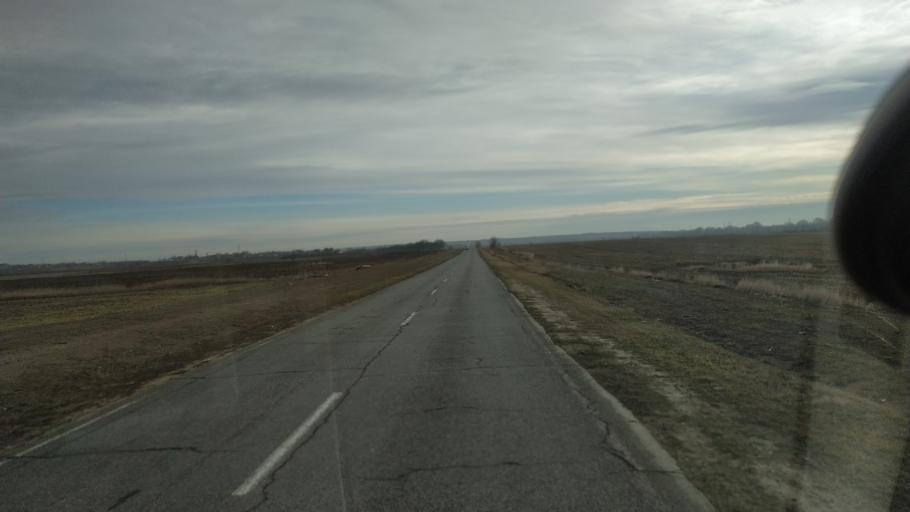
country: MD
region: Chisinau
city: Vadul lui Voda
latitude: 47.1521
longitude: 29.0956
